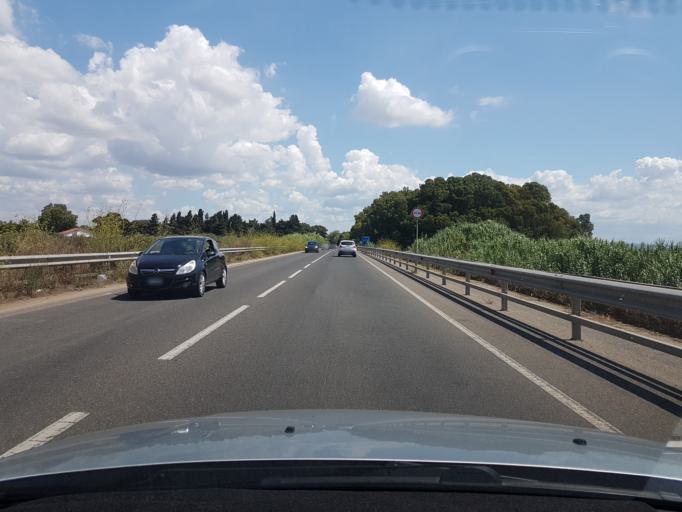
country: IT
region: Sardinia
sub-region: Provincia di Oristano
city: Solanas
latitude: 39.9201
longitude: 8.5623
